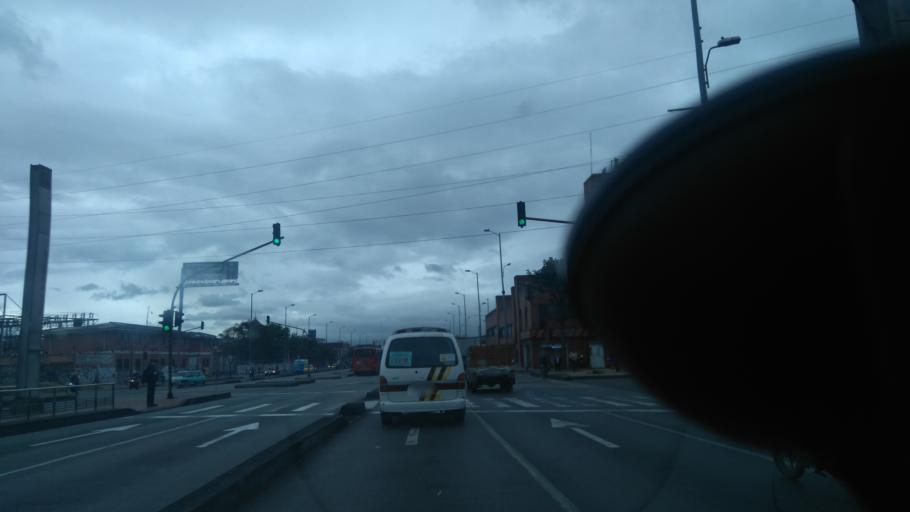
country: CO
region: Bogota D.C.
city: Bogota
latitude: 4.6208
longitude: -74.0990
